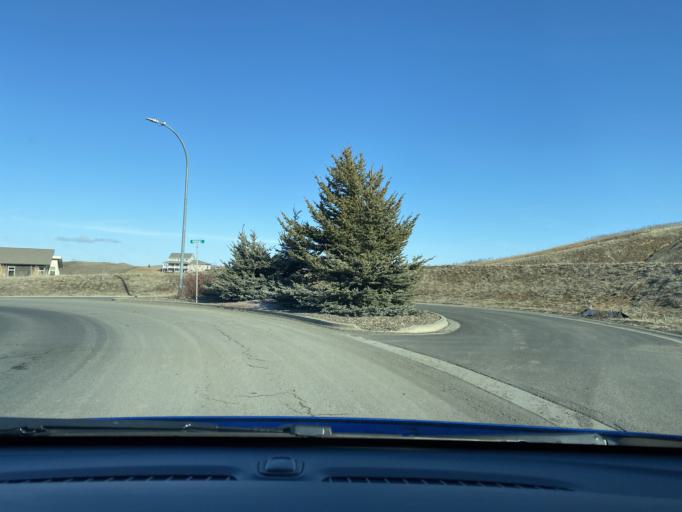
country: US
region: Washington
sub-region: Whitman County
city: Pullman
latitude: 46.7520
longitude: -117.1570
